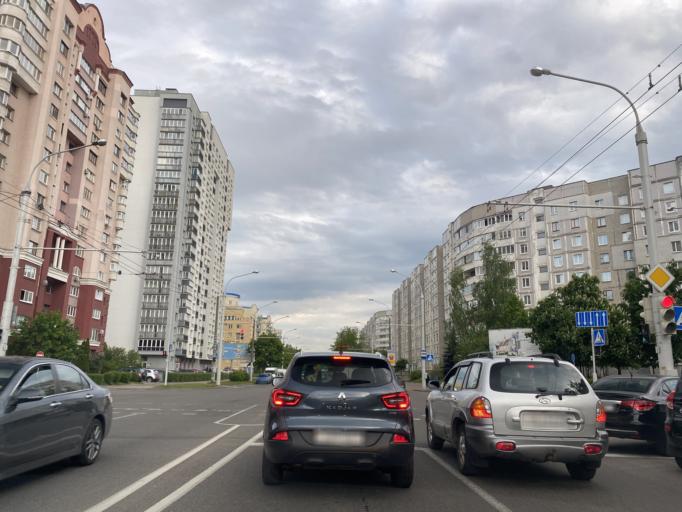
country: BY
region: Minsk
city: Borovlyany
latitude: 53.9518
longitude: 27.6909
